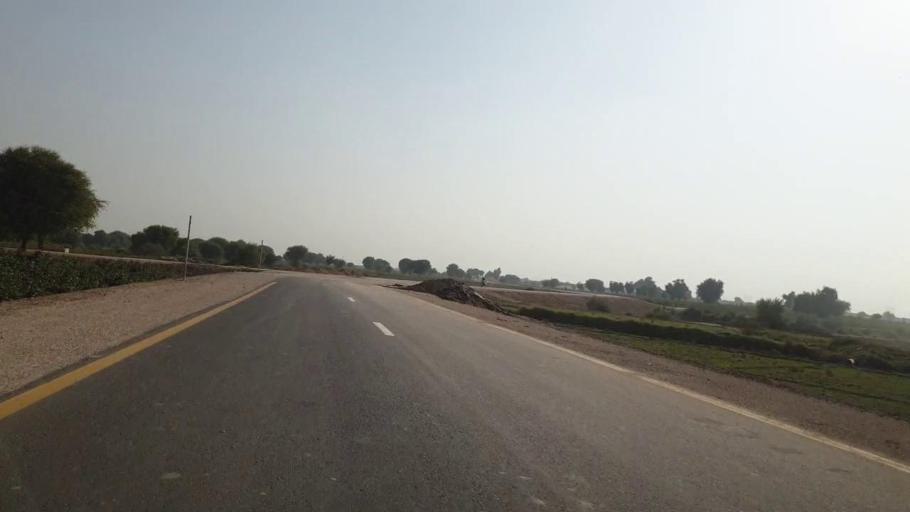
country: PK
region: Sindh
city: Bhan
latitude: 26.5077
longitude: 67.7842
